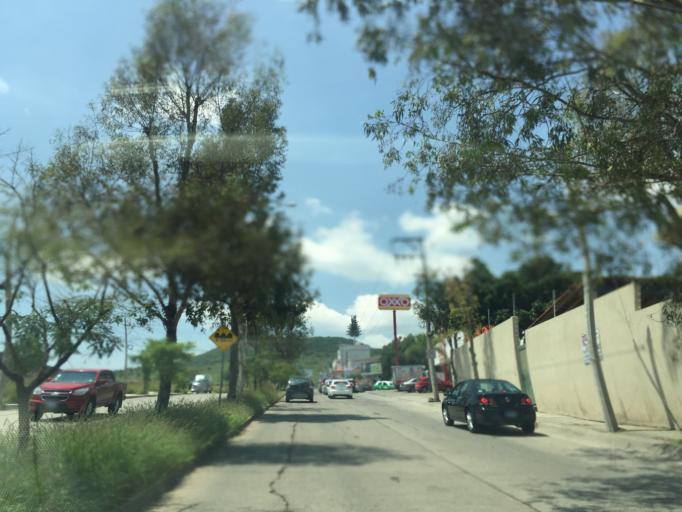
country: MX
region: Guanajuato
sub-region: Leon
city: La Ermita
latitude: 21.1584
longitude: -101.7037
